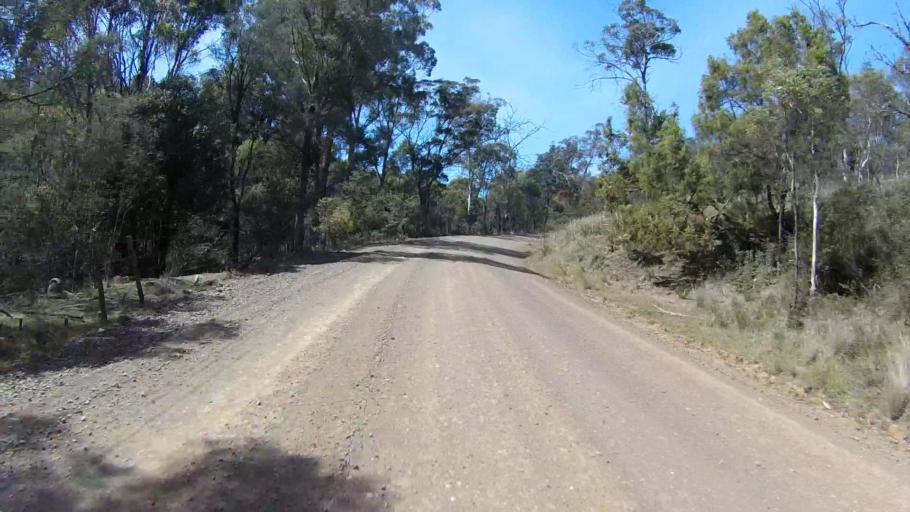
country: AU
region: Tasmania
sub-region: Sorell
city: Sorell
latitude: -42.6438
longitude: 147.7409
